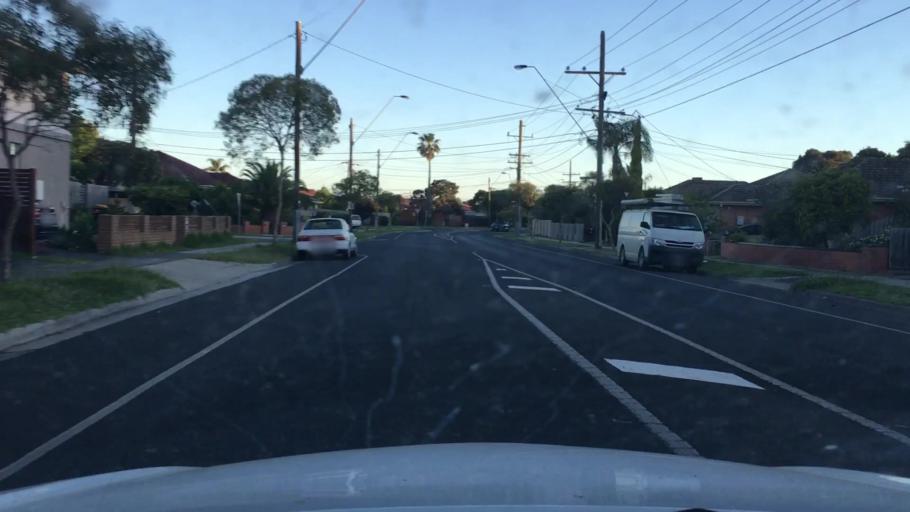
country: AU
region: Victoria
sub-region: Greater Dandenong
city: Keysborough
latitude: -37.9826
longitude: 145.1685
